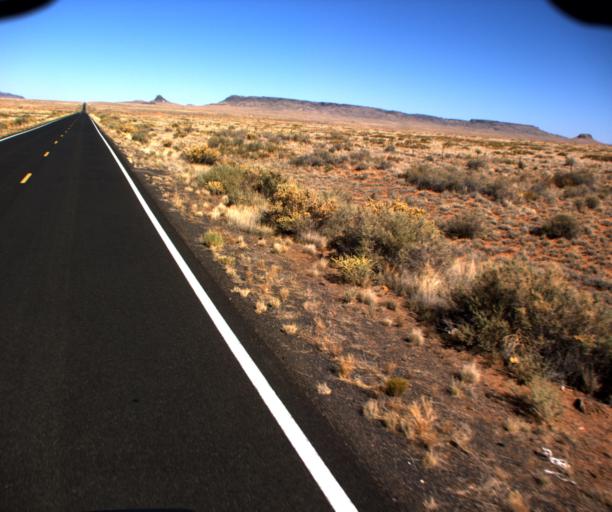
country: US
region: Arizona
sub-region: Navajo County
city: Dilkon
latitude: 35.3458
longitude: -110.4241
